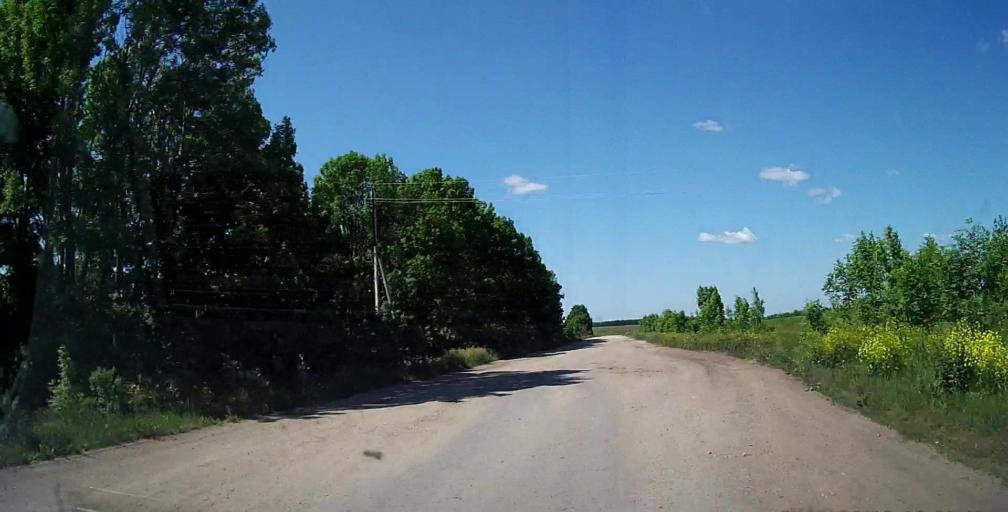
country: RU
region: Tula
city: Kurkino
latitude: 53.2016
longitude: 38.5875
